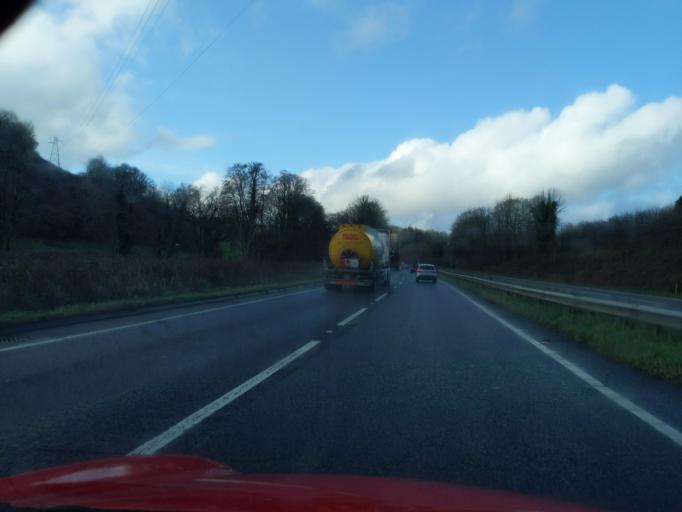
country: GB
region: England
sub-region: Cornwall
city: Liskeard
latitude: 50.4186
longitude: -4.3983
